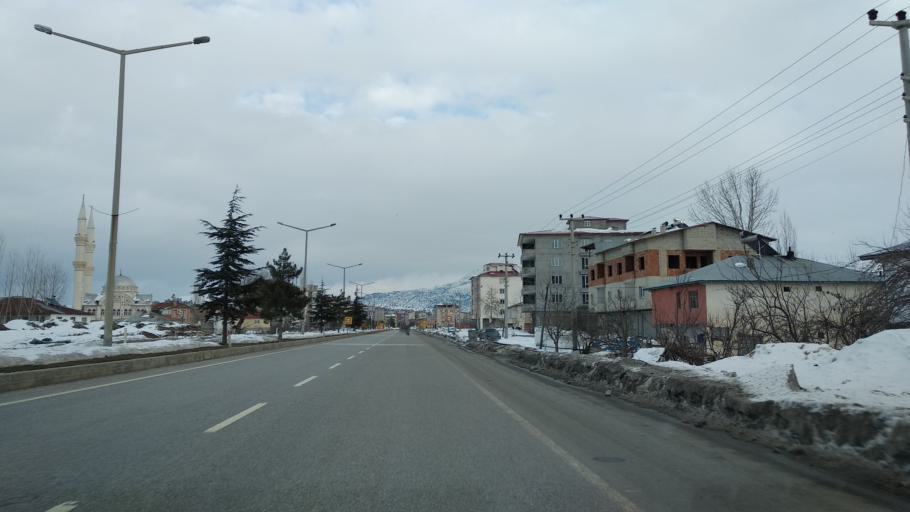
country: TR
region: Kahramanmaras
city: Goksun
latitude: 38.0264
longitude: 36.4912
